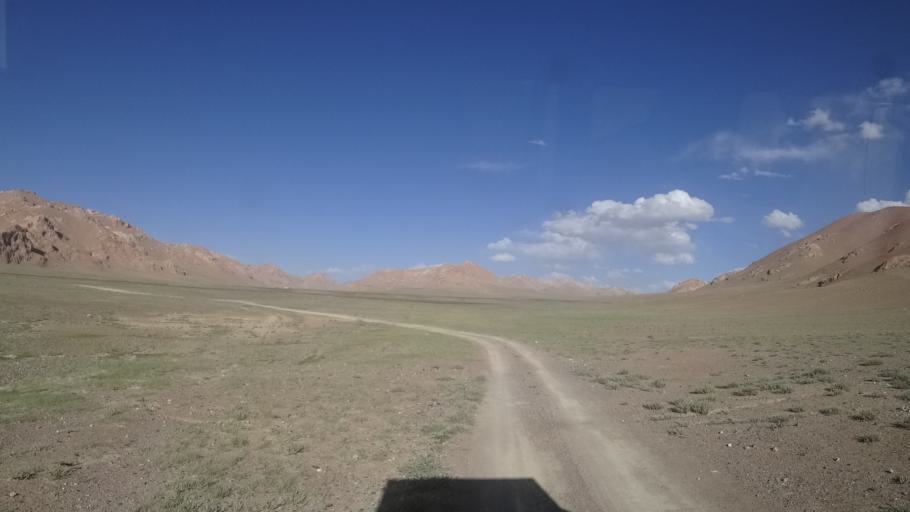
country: TJ
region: Gorno-Badakhshan
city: Murghob
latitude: 37.6561
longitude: 74.1680
